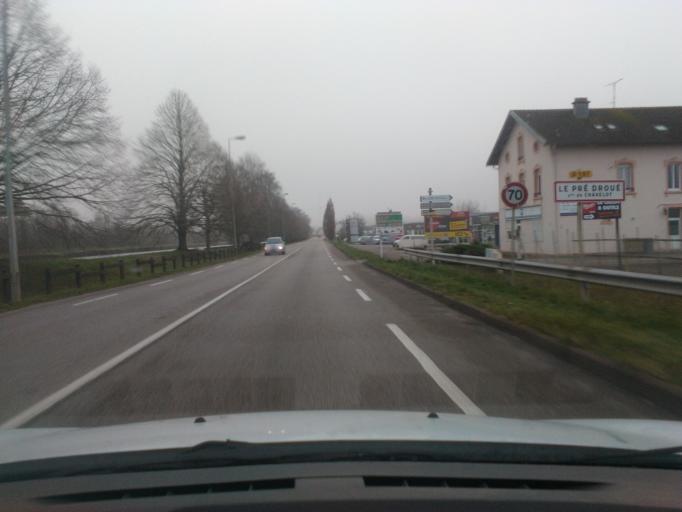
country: FR
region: Lorraine
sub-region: Departement des Vosges
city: Chavelot
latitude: 48.2206
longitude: 6.4367
